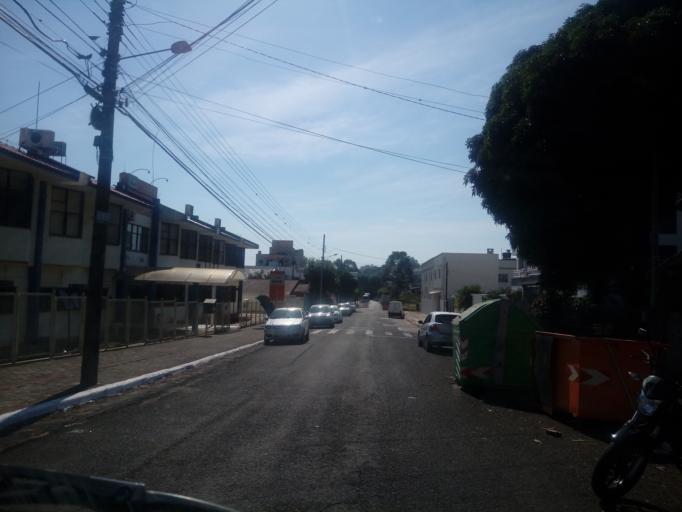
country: BR
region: Santa Catarina
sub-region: Chapeco
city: Chapeco
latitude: -27.0881
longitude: -52.6255
